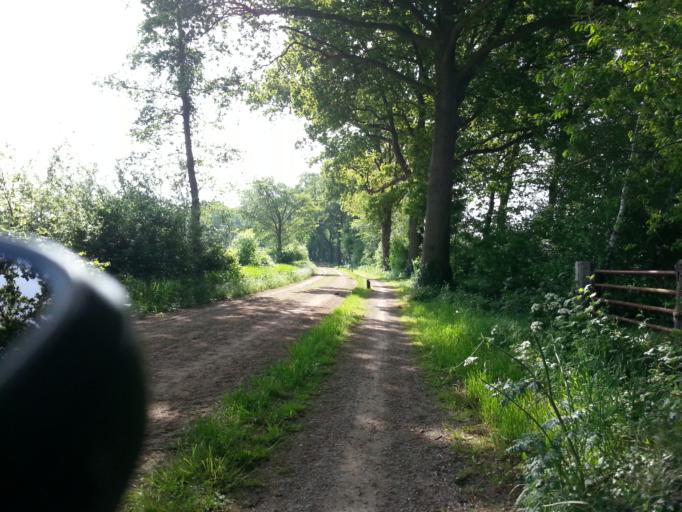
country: NL
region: Gelderland
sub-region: Berkelland
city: Neede
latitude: 52.1044
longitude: 6.6127
